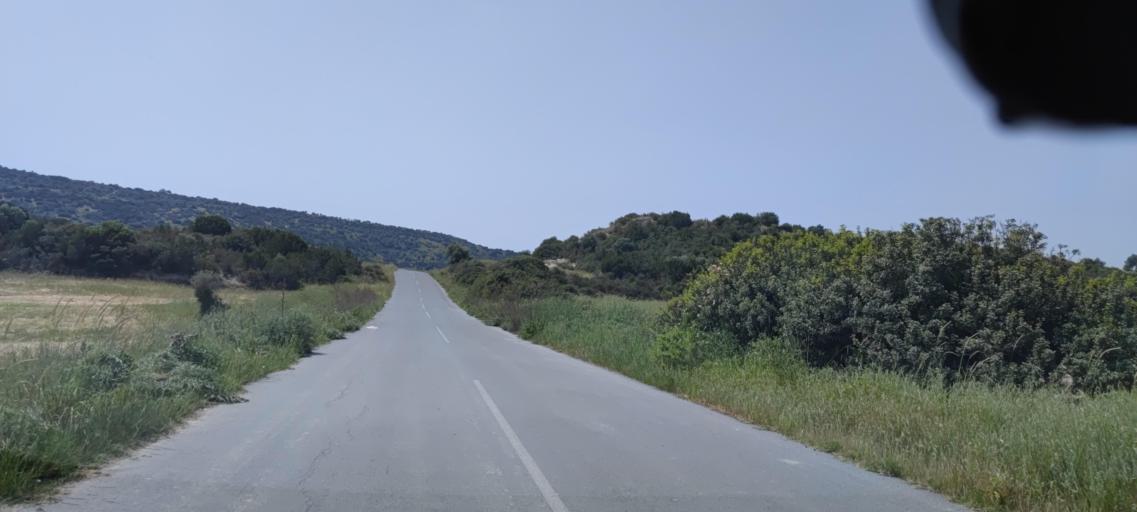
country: CY
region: Ammochostos
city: Leonarisso
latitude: 35.5107
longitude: 34.2664
